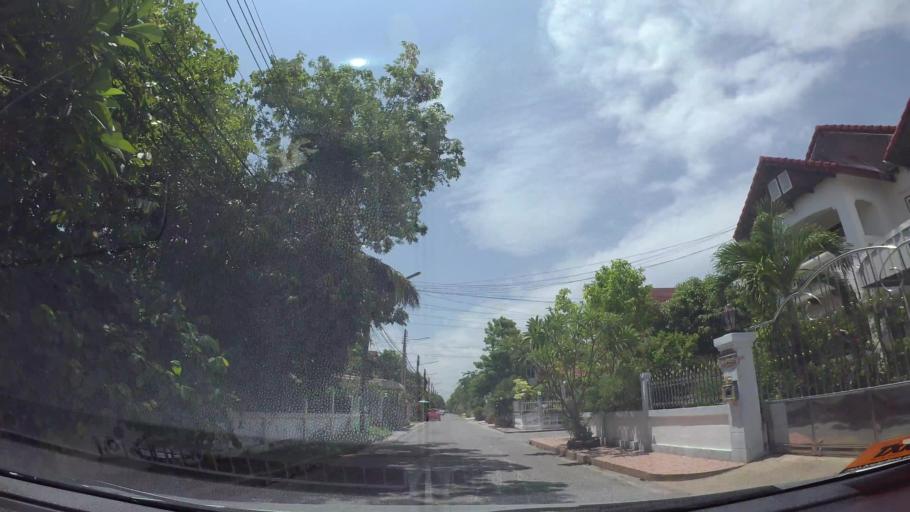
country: TH
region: Chon Buri
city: Chon Buri
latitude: 13.3333
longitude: 100.9378
